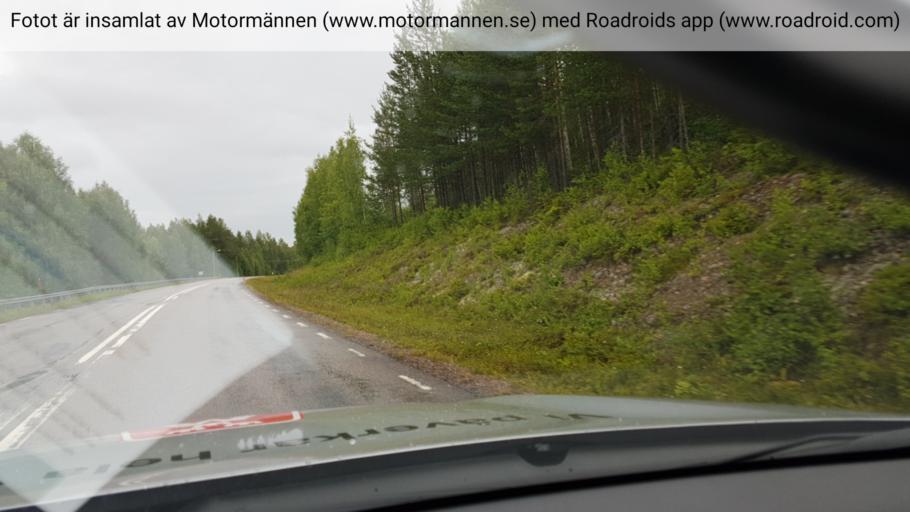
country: SE
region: Norrbotten
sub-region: Alvsbyns Kommun
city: AElvsbyn
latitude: 66.1482
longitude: 20.8747
